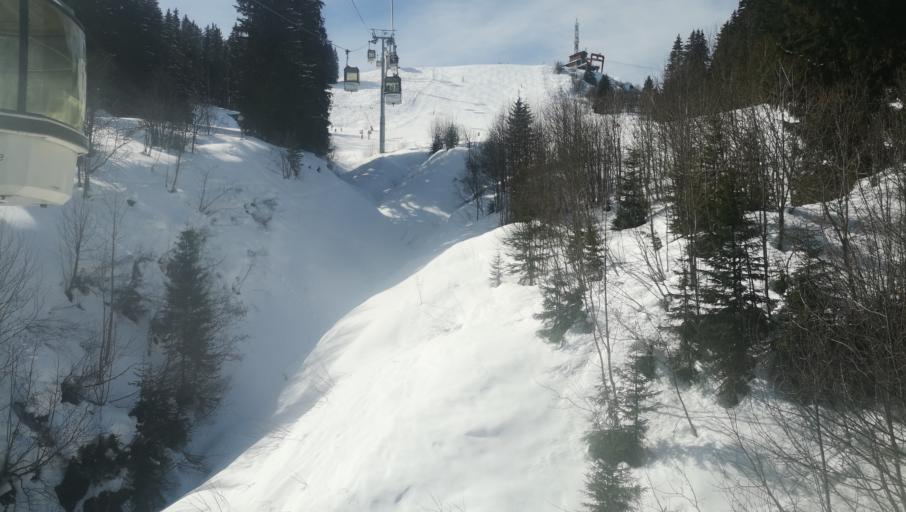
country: FR
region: Rhone-Alpes
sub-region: Departement de la Haute-Savoie
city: Megeve
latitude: 45.8361
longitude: 6.6174
